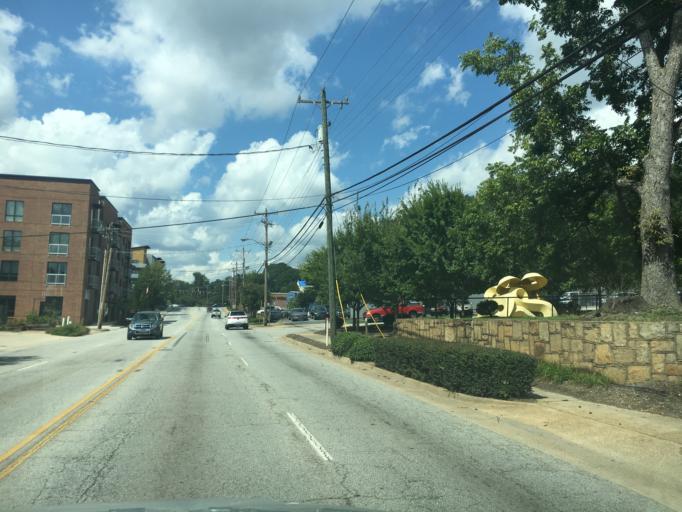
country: US
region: South Carolina
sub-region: Greenville County
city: Greenville
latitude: 34.8608
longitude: -82.3914
